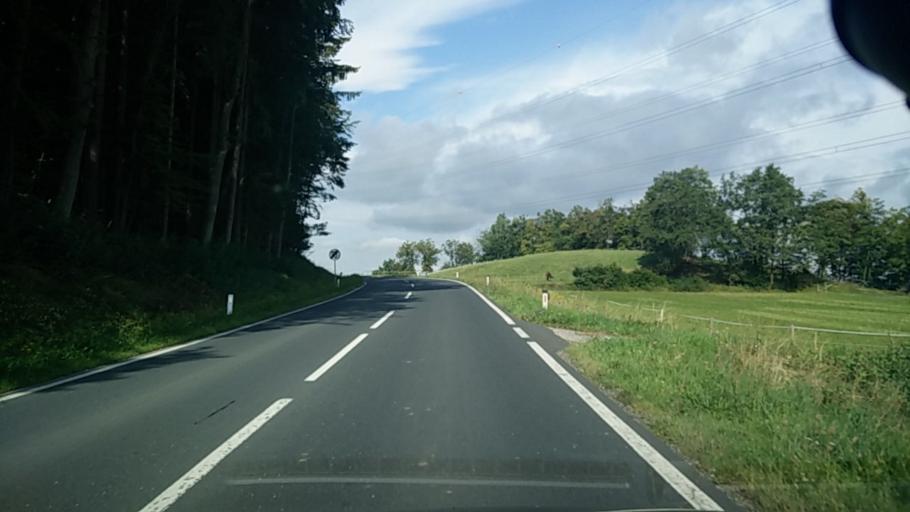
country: AT
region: Carinthia
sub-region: Politischer Bezirk Volkermarkt
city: Gallizien
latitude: 46.6159
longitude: 14.5636
